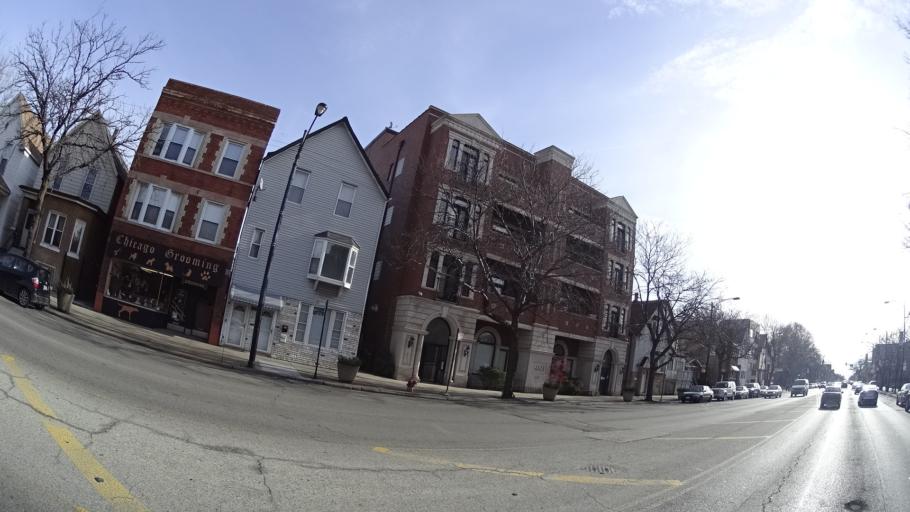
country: US
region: Illinois
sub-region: Cook County
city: Lincolnwood
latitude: 41.9640
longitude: -87.6888
